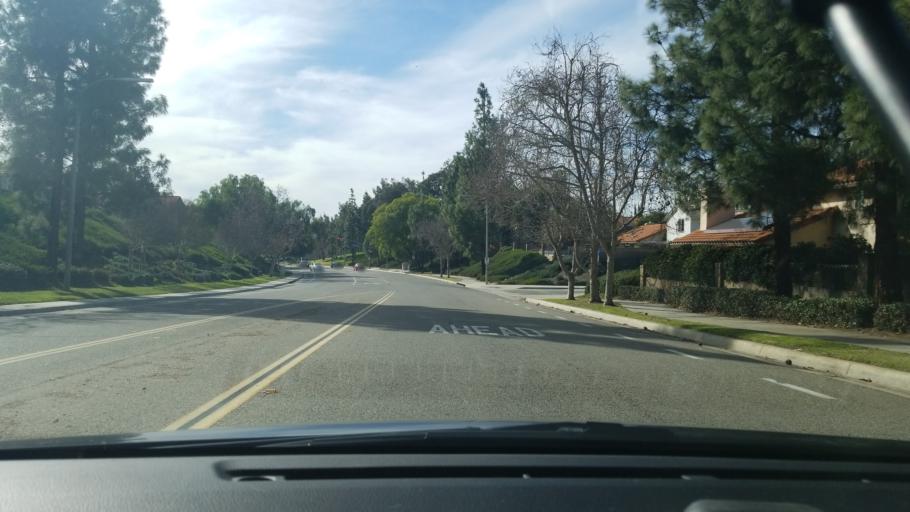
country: US
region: California
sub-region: Riverside County
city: Murrieta Hot Springs
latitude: 33.5627
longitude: -117.1746
